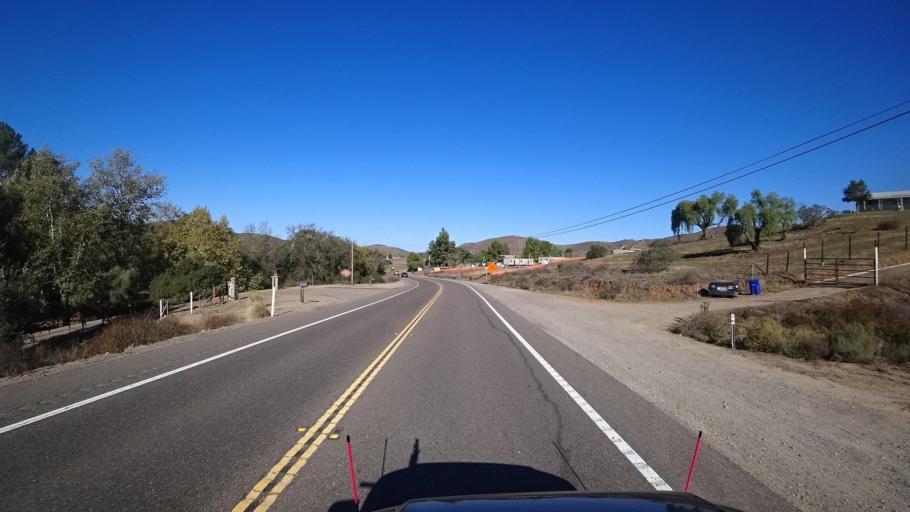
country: US
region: California
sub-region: San Diego County
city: Jamul
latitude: 32.6414
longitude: -116.7736
